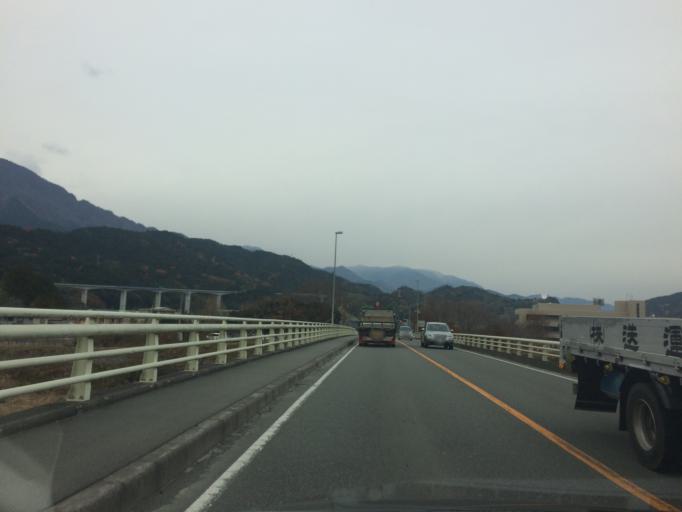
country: JP
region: Shizuoka
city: Fujinomiya
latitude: 35.2404
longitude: 138.4873
